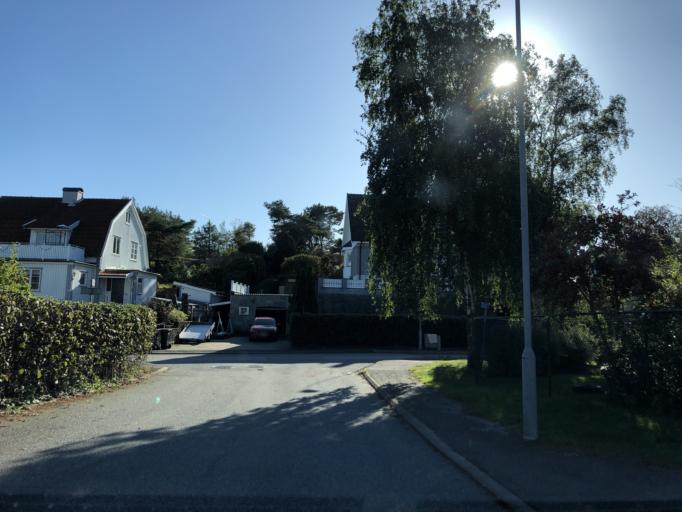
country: SE
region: Vaestra Goetaland
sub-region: Goteborg
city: Majorna
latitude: 57.6520
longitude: 11.8632
